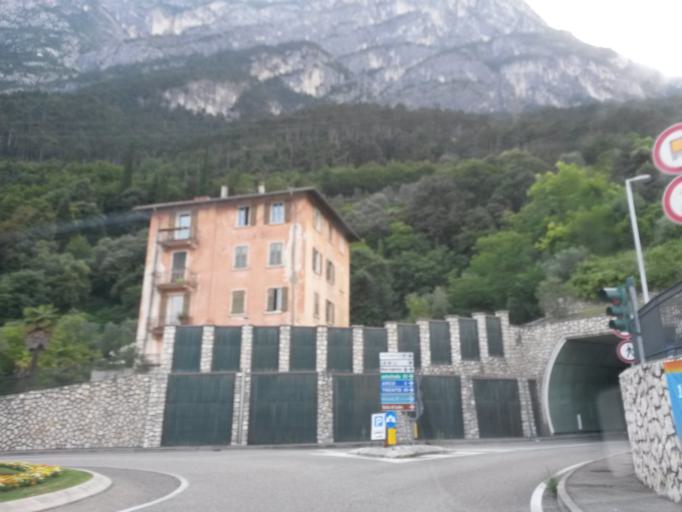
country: IT
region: Trentino-Alto Adige
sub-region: Provincia di Trento
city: Riva del Garda
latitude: 45.8823
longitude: 10.8410
